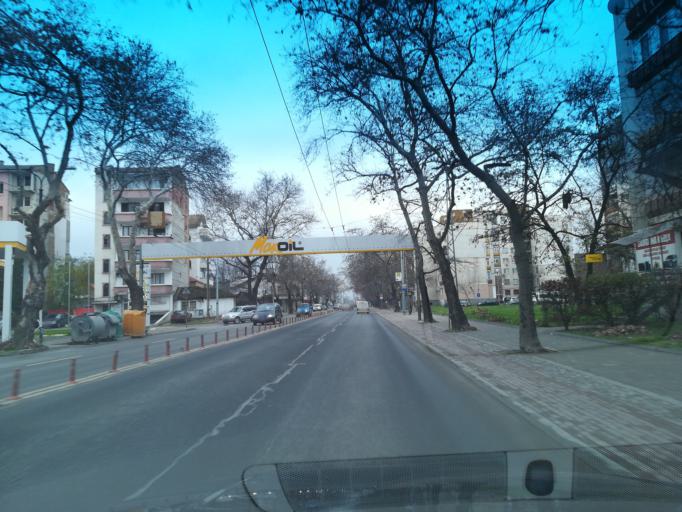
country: BG
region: Plovdiv
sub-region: Obshtina Plovdiv
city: Plovdiv
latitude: 42.1515
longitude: 24.7632
